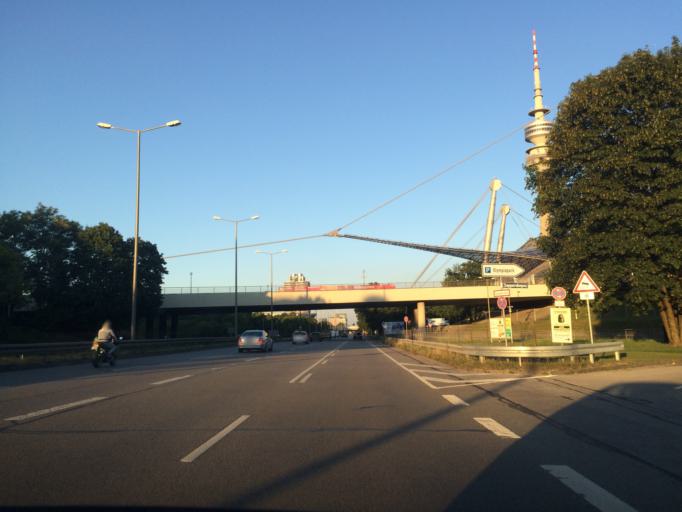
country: DE
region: Bavaria
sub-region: Upper Bavaria
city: Munich
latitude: 48.1761
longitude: 11.5462
